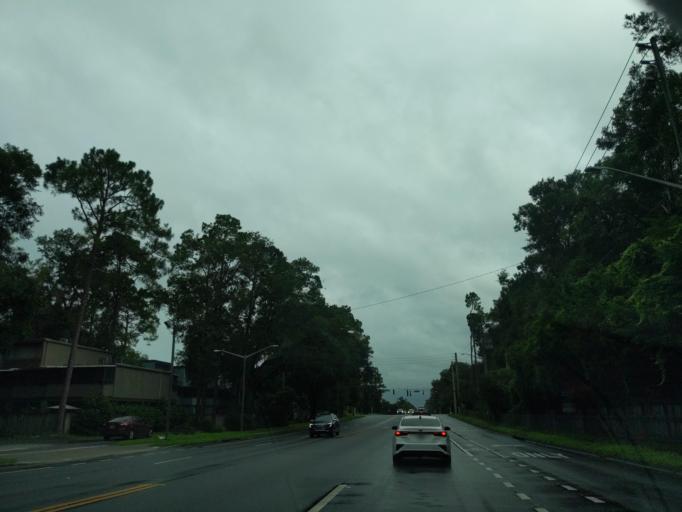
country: US
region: Florida
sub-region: Alachua County
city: Gainesville
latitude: 29.6467
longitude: -82.4225
